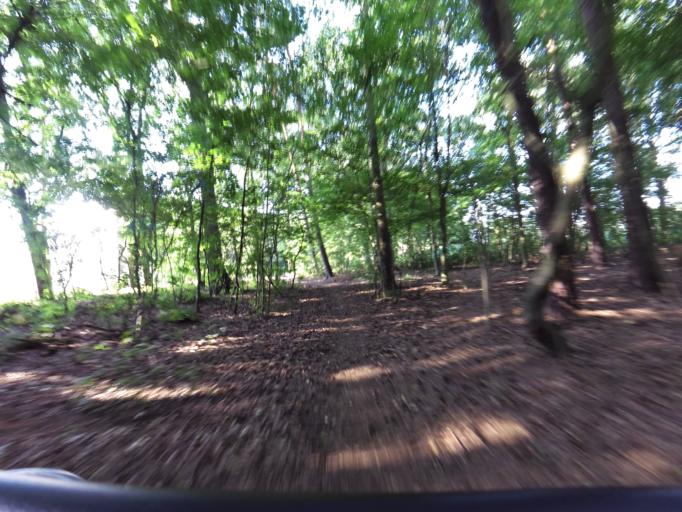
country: BE
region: Flanders
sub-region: Provincie Antwerpen
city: Stabroek
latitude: 51.3655
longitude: 4.4035
